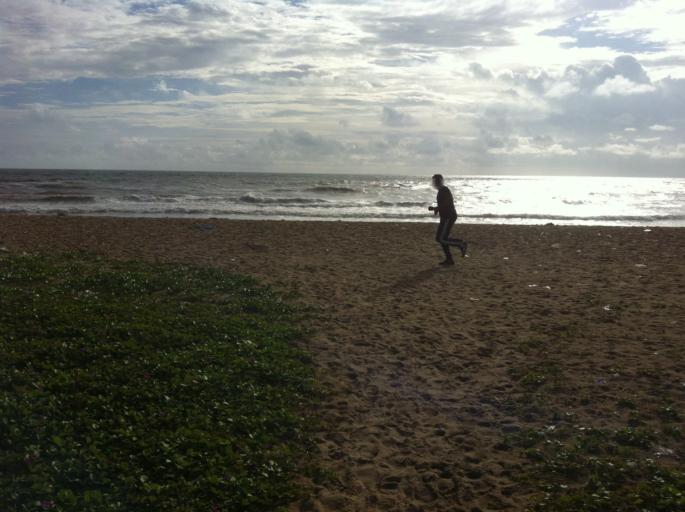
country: IN
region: Tamil Nadu
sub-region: Kancheepuram
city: Palavakkam
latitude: 12.9789
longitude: 80.2675
